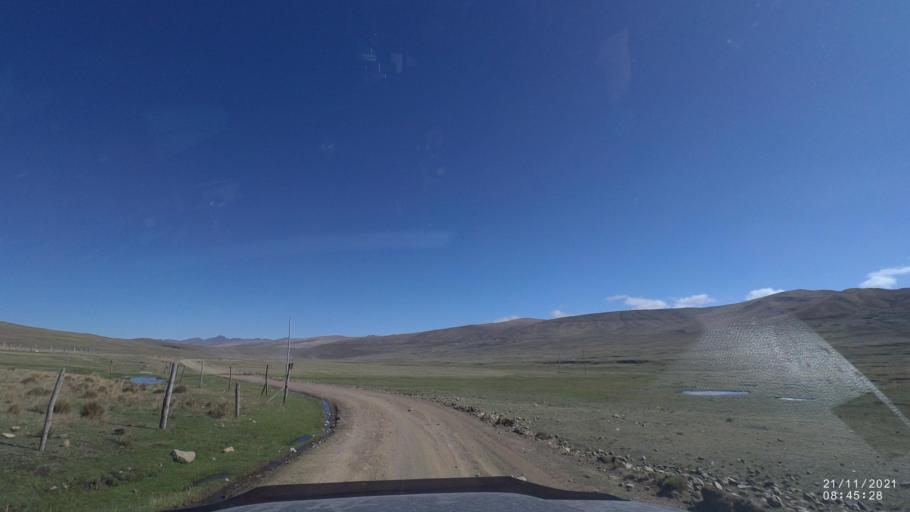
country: BO
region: Cochabamba
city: Cochabamba
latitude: -17.2485
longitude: -66.2318
